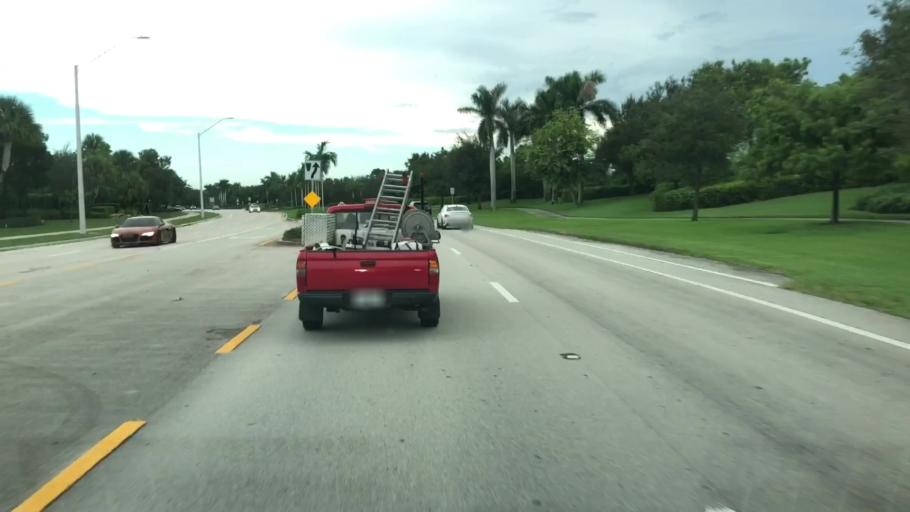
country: US
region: Florida
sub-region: Broward County
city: Parkland
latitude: 26.3222
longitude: -80.2787
